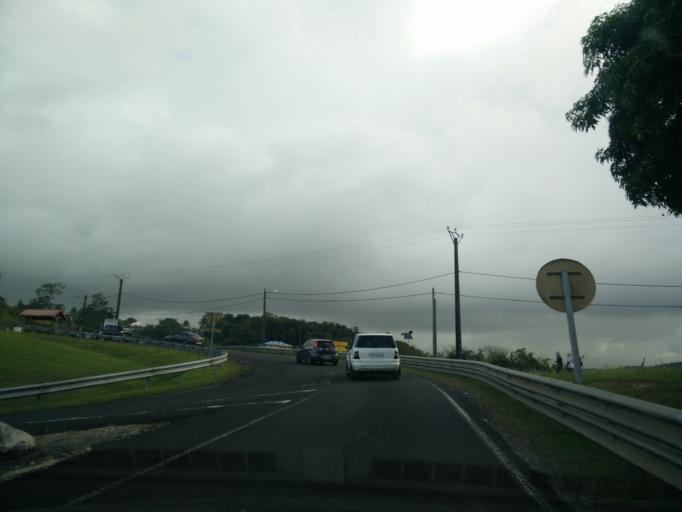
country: GP
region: Guadeloupe
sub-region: Guadeloupe
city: Petit-Bourg
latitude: 16.1975
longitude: -61.6062
